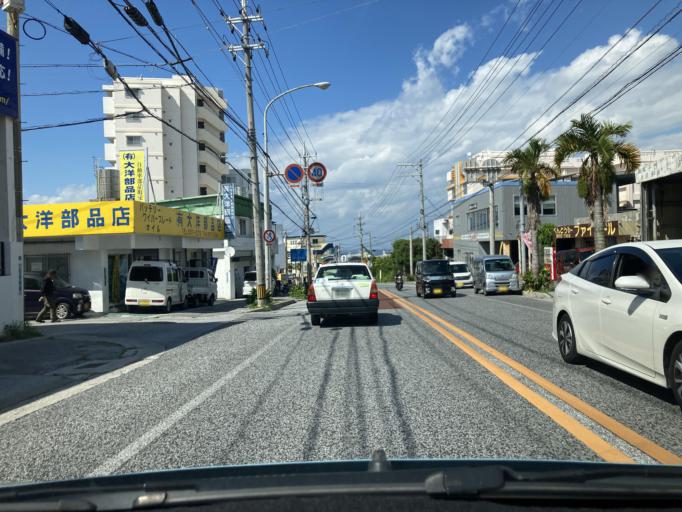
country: JP
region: Okinawa
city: Ginowan
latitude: 26.2640
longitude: 127.7395
